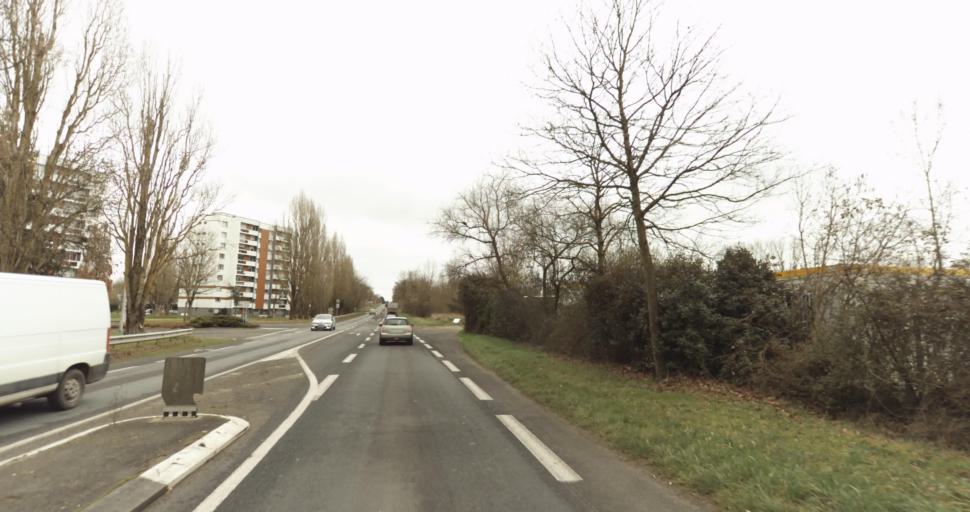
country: FR
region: Pays de la Loire
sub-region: Departement de Maine-et-Loire
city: Varrains
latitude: 47.2387
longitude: -0.0787
